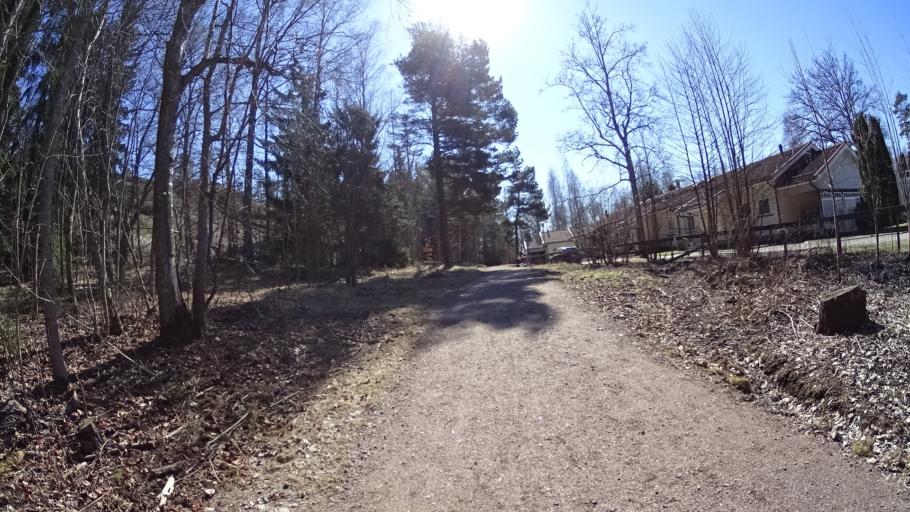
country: FI
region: Uusimaa
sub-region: Helsinki
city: Koukkuniemi
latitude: 60.1442
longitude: 24.7007
